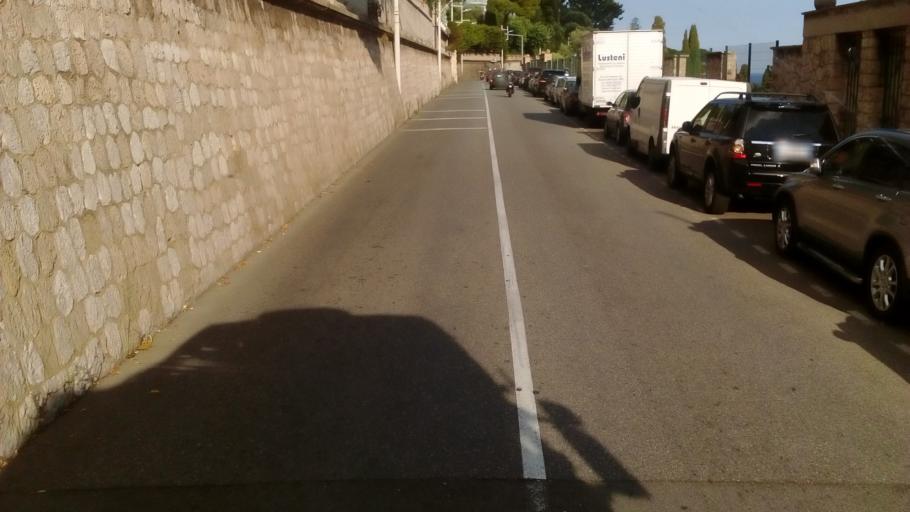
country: MC
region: Commune de Monaco
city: Saint-Roman
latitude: 43.7531
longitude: 7.4406
